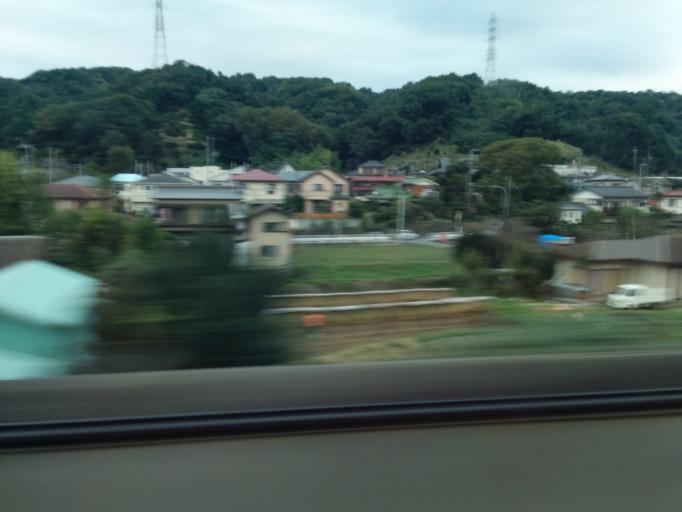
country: JP
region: Kanagawa
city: Oiso
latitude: 35.3250
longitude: 139.2893
